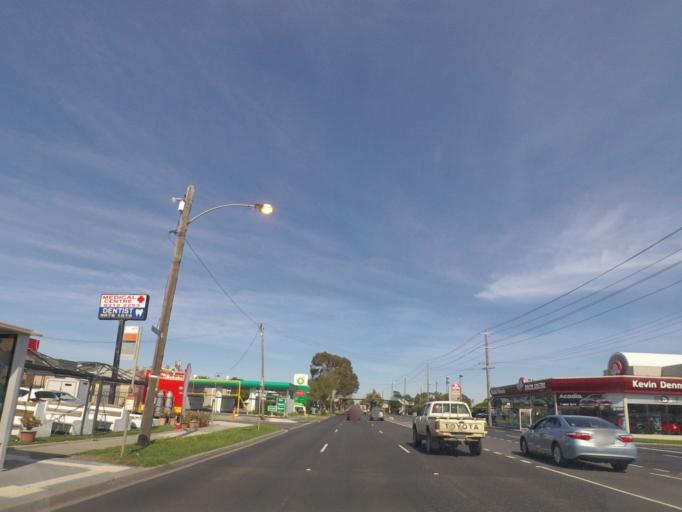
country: AU
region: Victoria
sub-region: Maribyrnong
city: Braybrook
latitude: -37.7804
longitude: 144.8576
